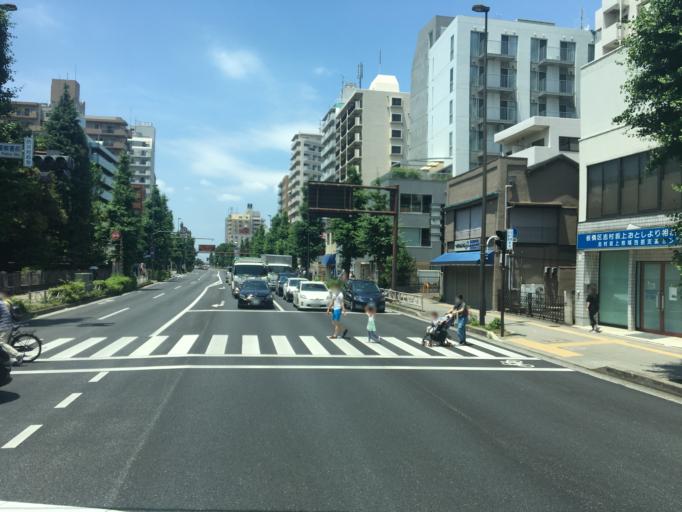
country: JP
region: Saitama
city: Kawaguchi
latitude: 35.7731
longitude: 139.6985
